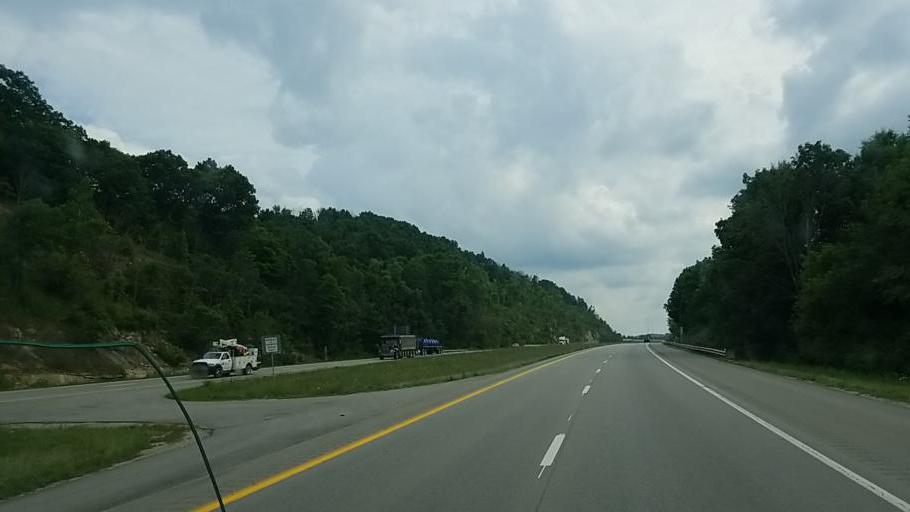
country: US
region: Ohio
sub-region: Guernsey County
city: Cambridge
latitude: 40.0121
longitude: -81.5595
